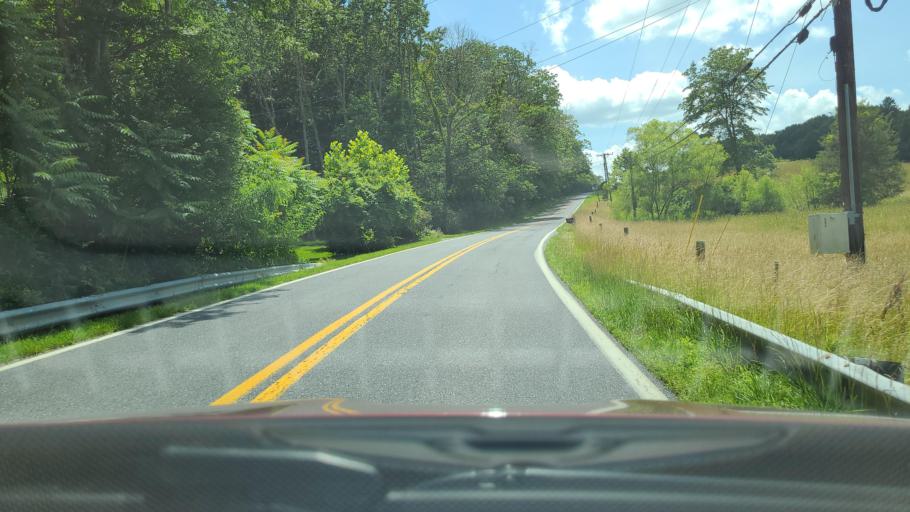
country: US
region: Maryland
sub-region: Montgomery County
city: Clarksburg
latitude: 39.2529
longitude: -77.2669
